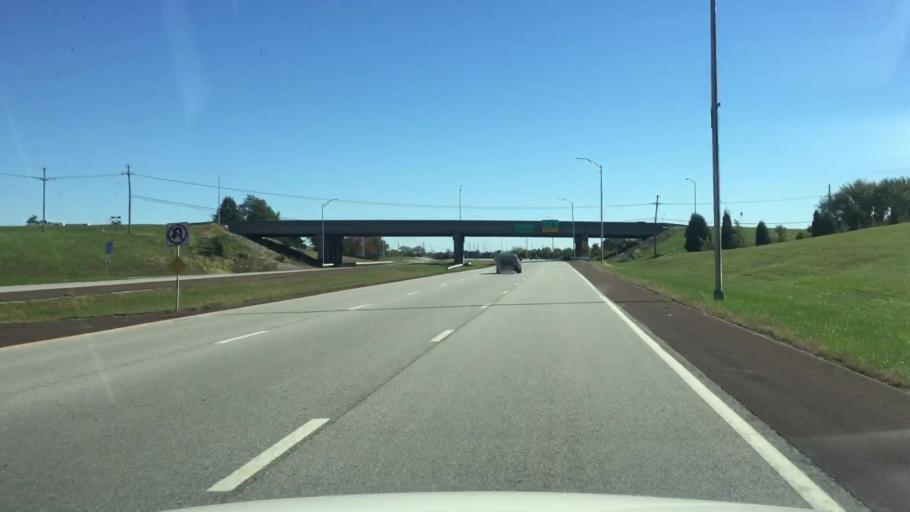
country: US
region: Kansas
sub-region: Johnson County
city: Shawnee
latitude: 39.0086
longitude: -94.7724
